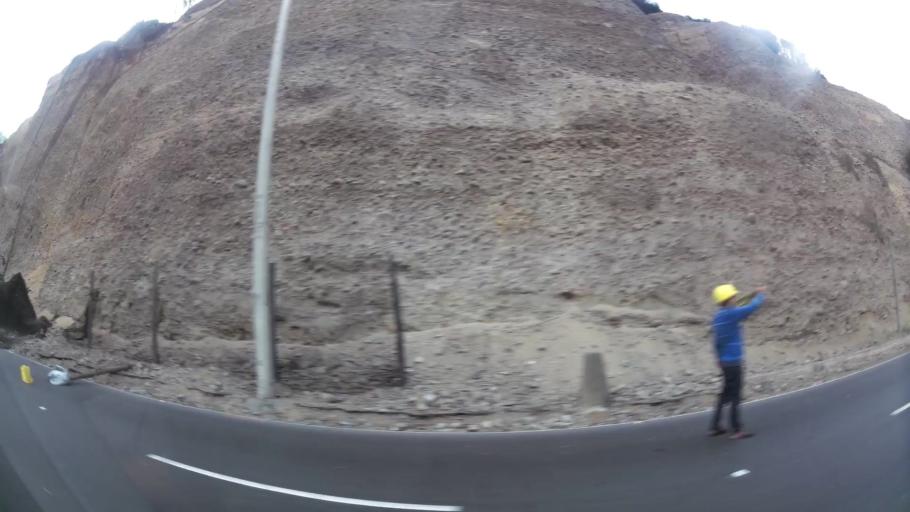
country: PE
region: Lima
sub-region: Lima
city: Surco
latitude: -12.1543
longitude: -77.0249
